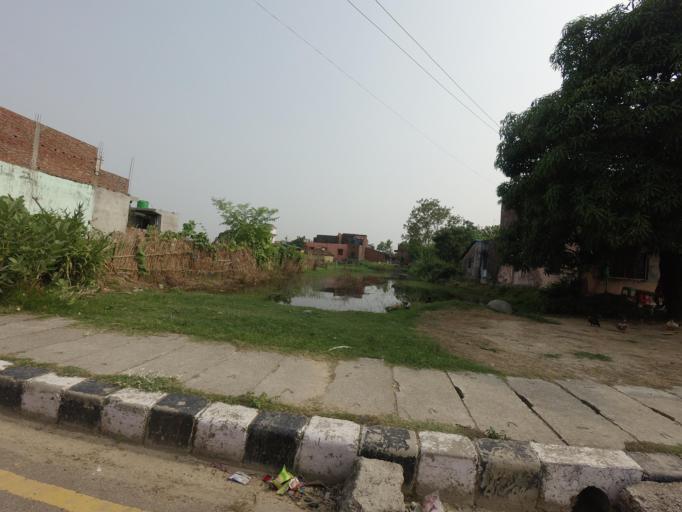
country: NP
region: Western Region
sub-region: Lumbini Zone
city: Bhairahawa
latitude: 27.5180
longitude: 83.4614
